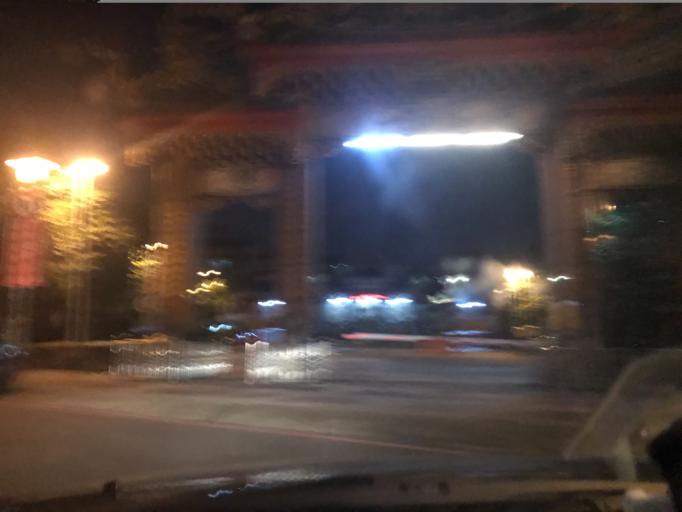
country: TW
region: Taiwan
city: Taoyuan City
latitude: 24.9451
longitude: 121.2142
